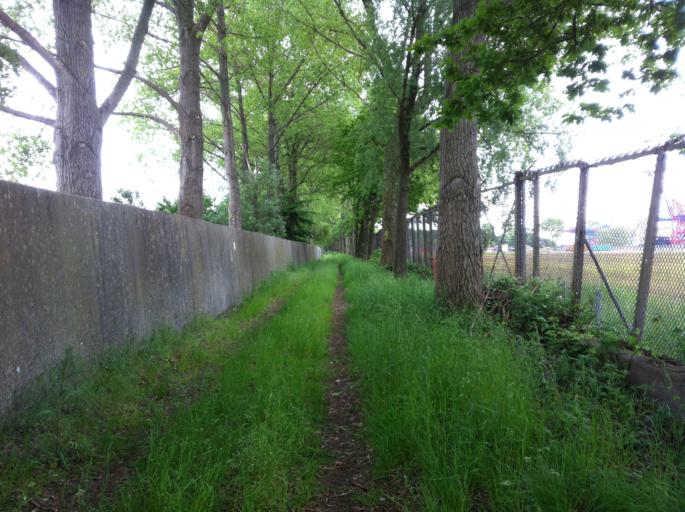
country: DE
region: Hamburg
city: Altona
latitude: 53.5397
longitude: 9.8879
